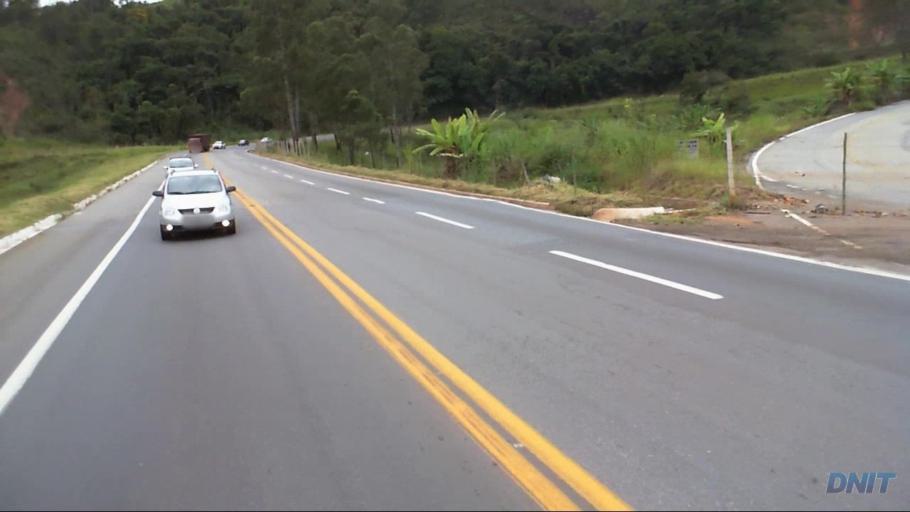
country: BR
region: Minas Gerais
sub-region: Joao Monlevade
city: Joao Monlevade
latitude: -19.8566
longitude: -43.2269
